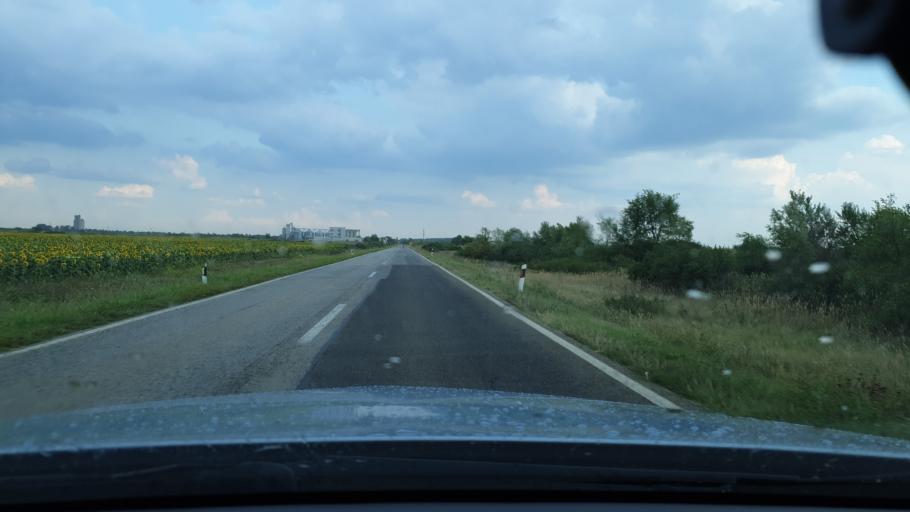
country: RS
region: Autonomna Pokrajina Vojvodina
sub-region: Srednjebanatski Okrug
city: Secanj
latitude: 45.3735
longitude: 20.7440
